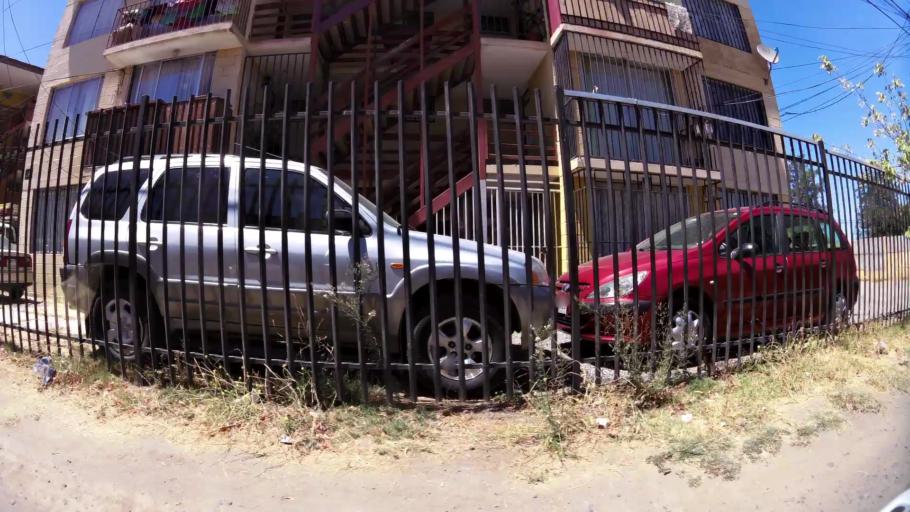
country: CL
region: O'Higgins
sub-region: Provincia de Cachapoal
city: Rancagua
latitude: -34.1581
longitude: -70.7538
